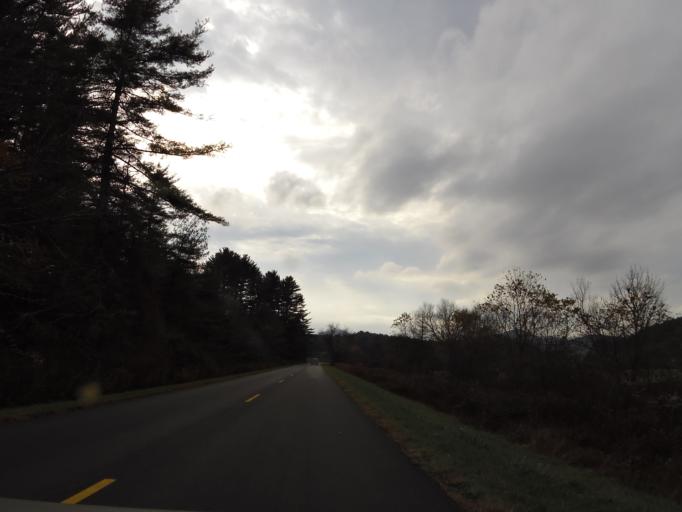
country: US
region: North Carolina
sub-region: Alleghany County
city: Sparta
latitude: 36.3931
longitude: -81.2328
